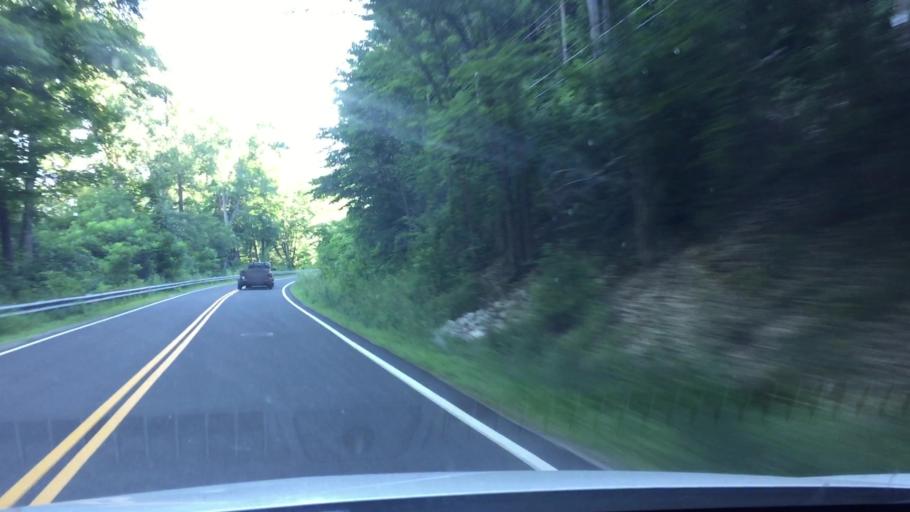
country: US
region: Massachusetts
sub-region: Berkshire County
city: Lee
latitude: 42.2815
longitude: -73.2400
